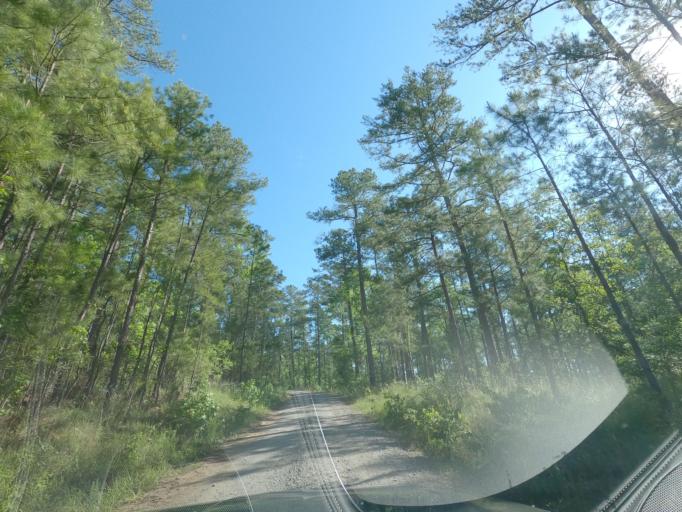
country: US
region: Georgia
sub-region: Columbia County
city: Evans
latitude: 33.6130
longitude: -82.1127
